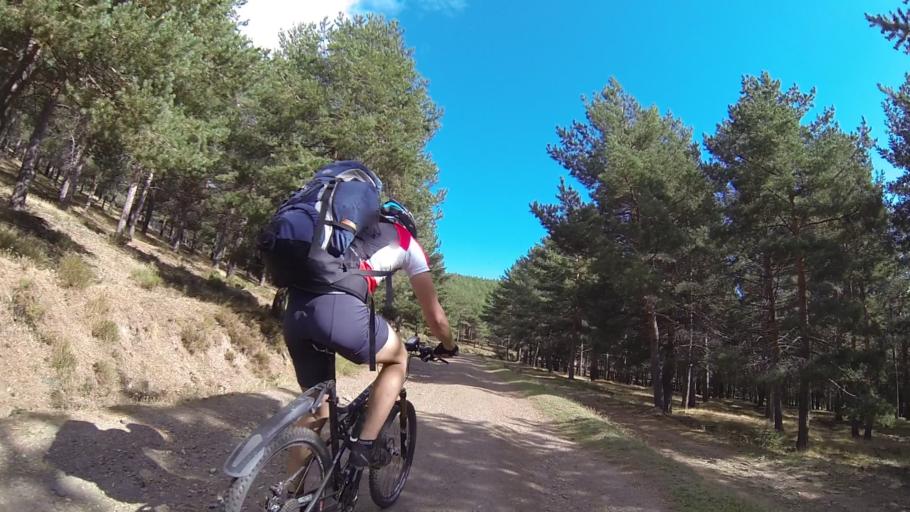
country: ES
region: Andalusia
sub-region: Provincia de Granada
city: Ferreira
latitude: 37.1132
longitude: -3.0282
